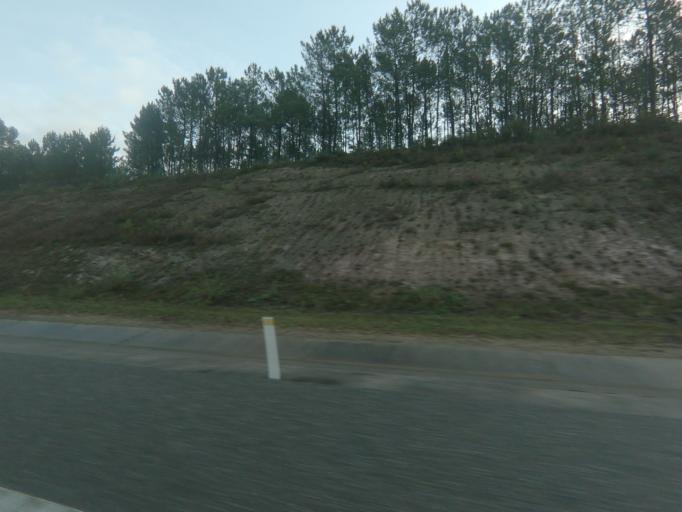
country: ES
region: Galicia
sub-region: Provincia de Pontevedra
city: Tui
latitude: 42.1013
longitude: -8.6441
